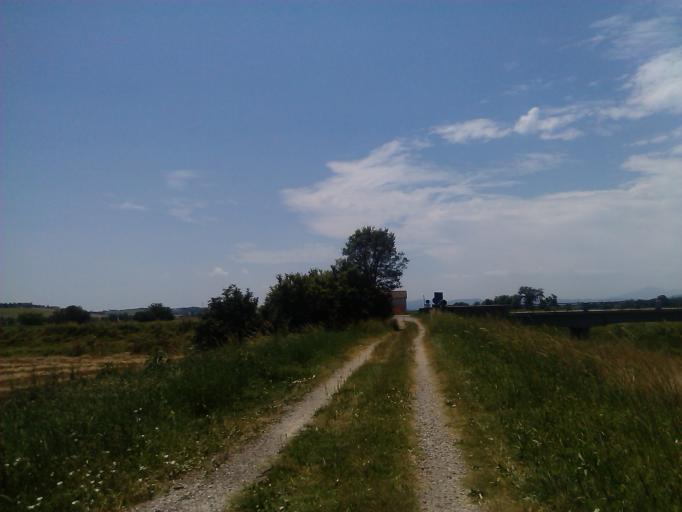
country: IT
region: Tuscany
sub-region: Province of Arezzo
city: Foiano della Chiana
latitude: 43.2821
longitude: 11.8411
